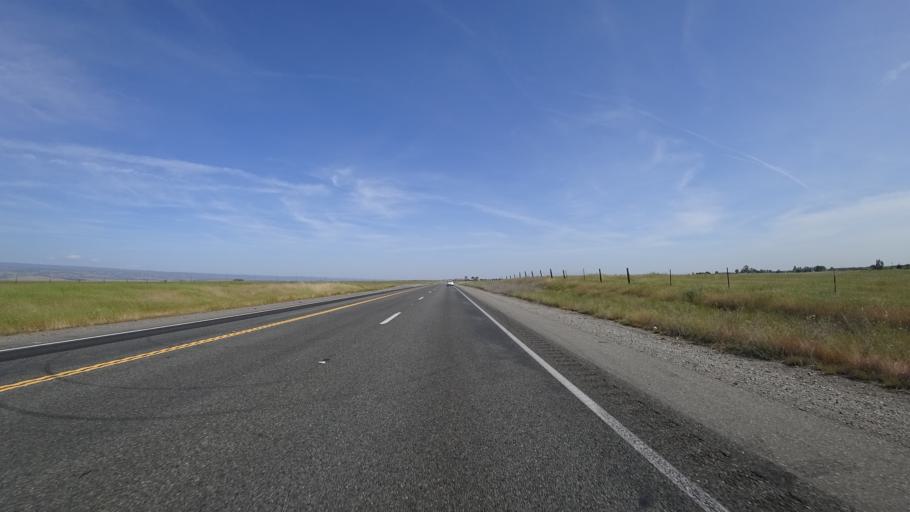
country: US
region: California
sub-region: Tehama County
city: Los Molinos
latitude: 39.9263
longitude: -122.0268
